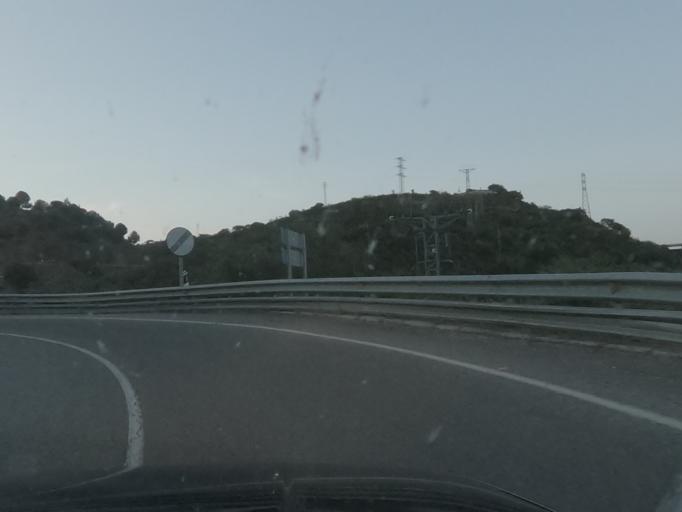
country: ES
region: Extremadura
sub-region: Provincia de Caceres
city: Alcantara
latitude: 39.7243
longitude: -6.8918
